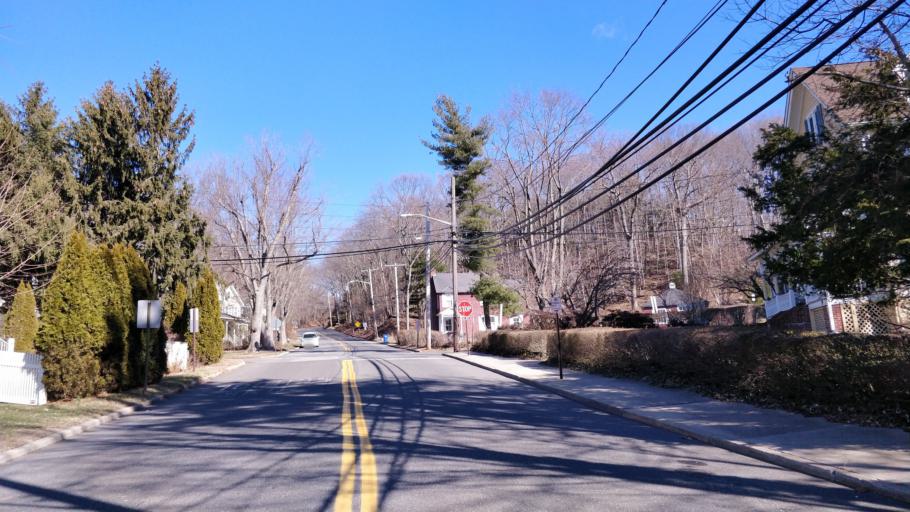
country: US
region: New York
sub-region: Suffolk County
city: Port Jefferson
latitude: 40.9419
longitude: -73.0623
